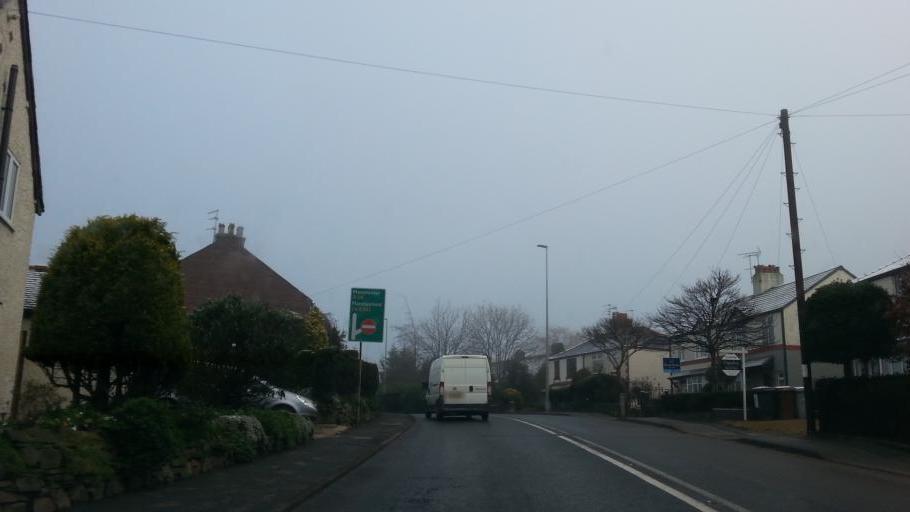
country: GB
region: England
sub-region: Cheshire East
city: Congleton
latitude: 53.1713
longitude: -2.2083
